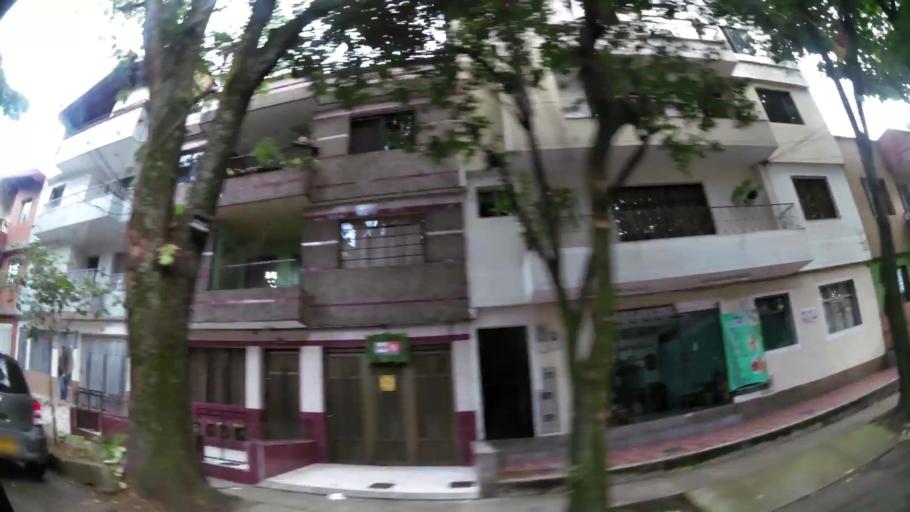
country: CO
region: Antioquia
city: Envigado
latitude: 6.1657
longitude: -75.5892
